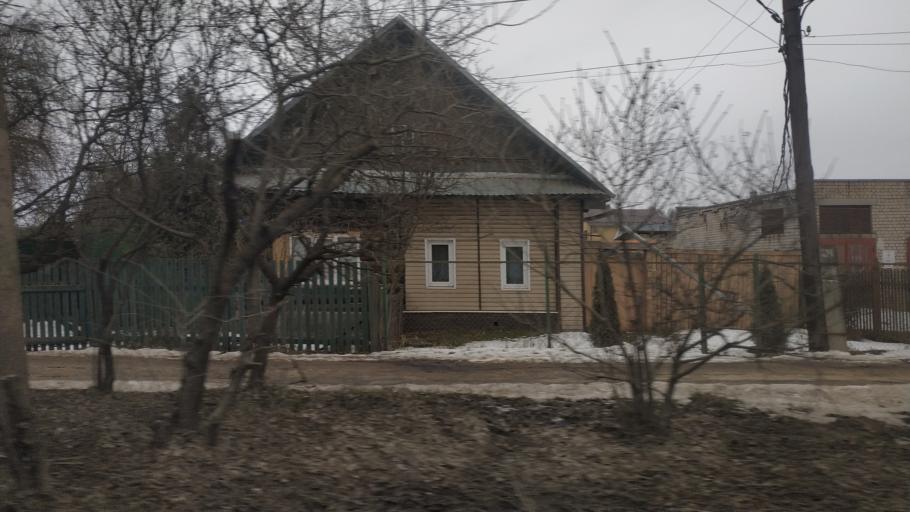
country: RU
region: Tverskaya
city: Tver
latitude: 56.8805
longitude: 35.8884
